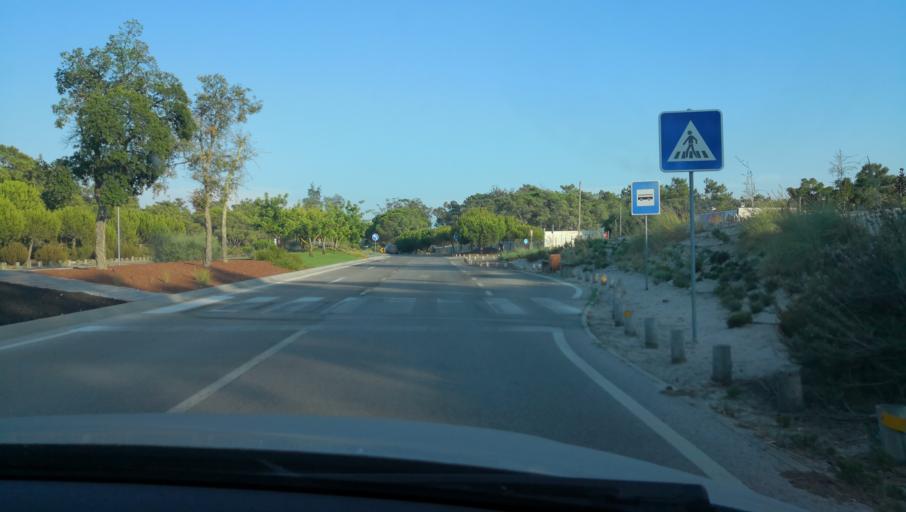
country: PT
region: Setubal
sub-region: Setubal
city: Setubal
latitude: 38.4659
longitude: -8.8738
